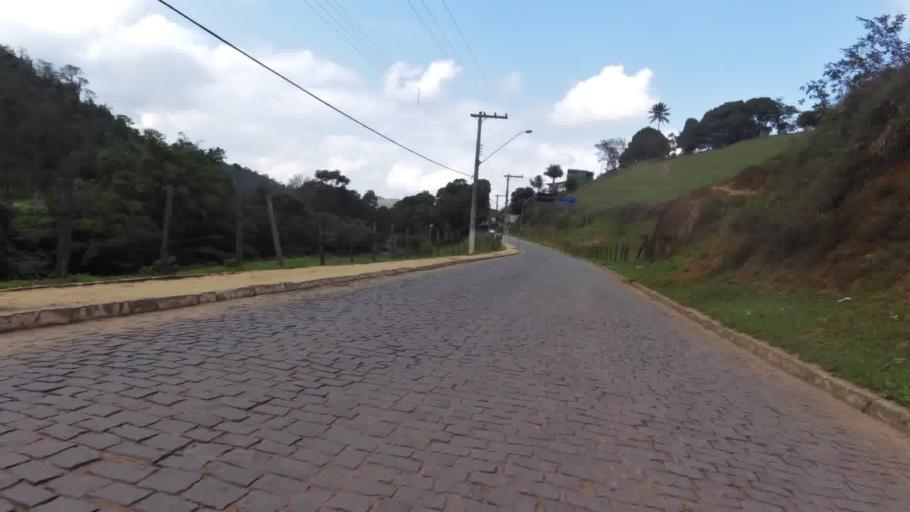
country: BR
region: Espirito Santo
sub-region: Alfredo Chaves
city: Alfredo Chaves
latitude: -20.6324
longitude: -40.7544
